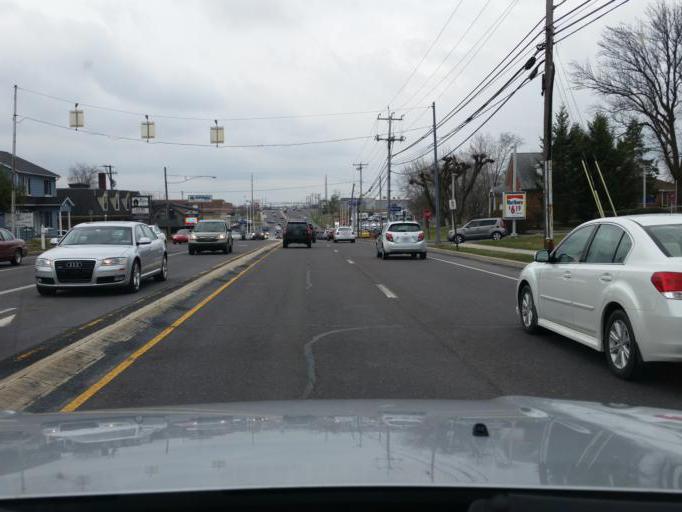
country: US
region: Pennsylvania
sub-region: Dauphin County
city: Paxtonia
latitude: 40.3161
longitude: -76.7971
